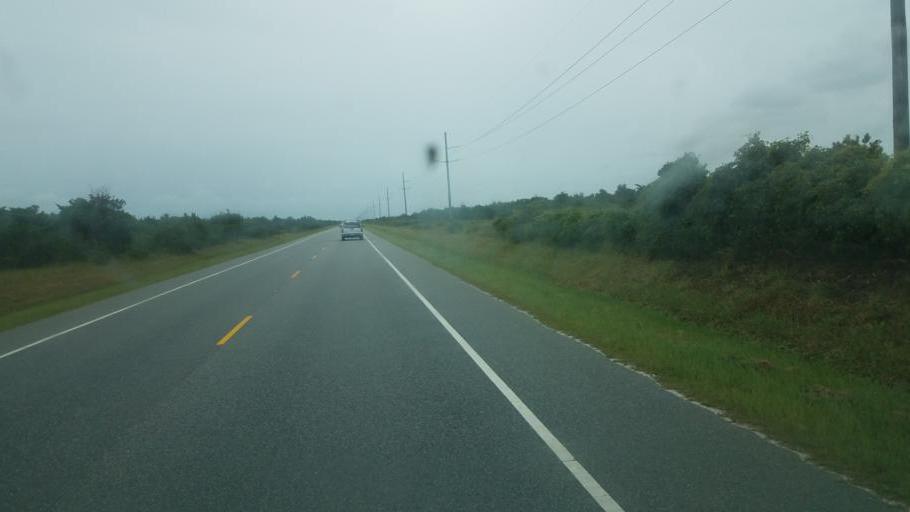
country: US
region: North Carolina
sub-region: Dare County
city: Buxton
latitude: 35.4986
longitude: -75.4799
